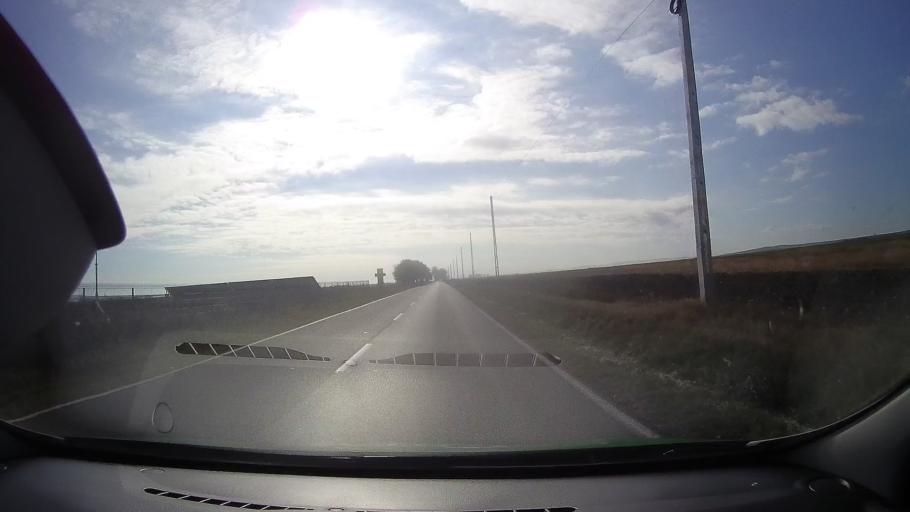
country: RO
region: Tulcea
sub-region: Comuna Valea Nucarilor
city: Agighiol
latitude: 45.0197
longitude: 28.8828
